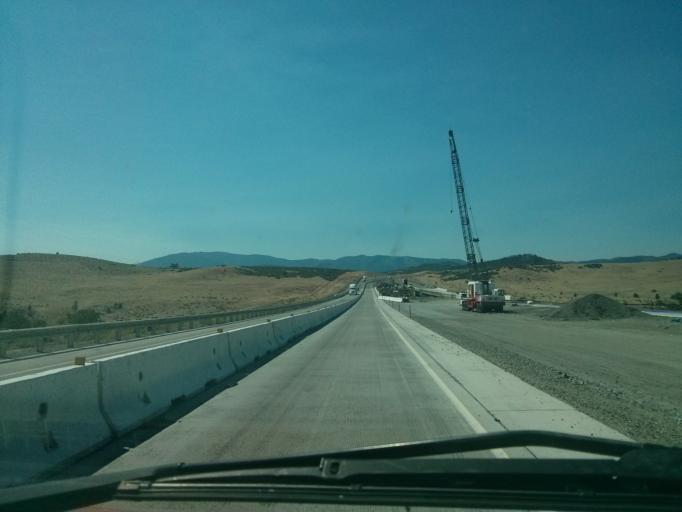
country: US
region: California
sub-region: Siskiyou County
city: Yreka
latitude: 41.7693
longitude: -122.5844
